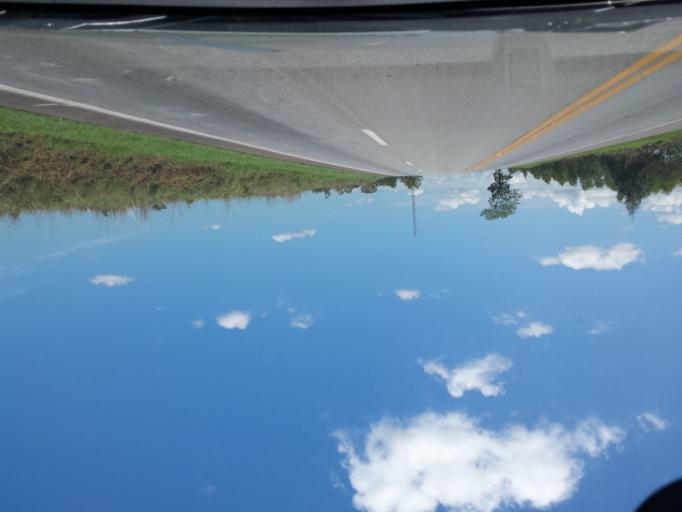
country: BR
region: Goias
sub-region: Cristalina
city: Cristalina
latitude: -16.5556
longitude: -47.7891
